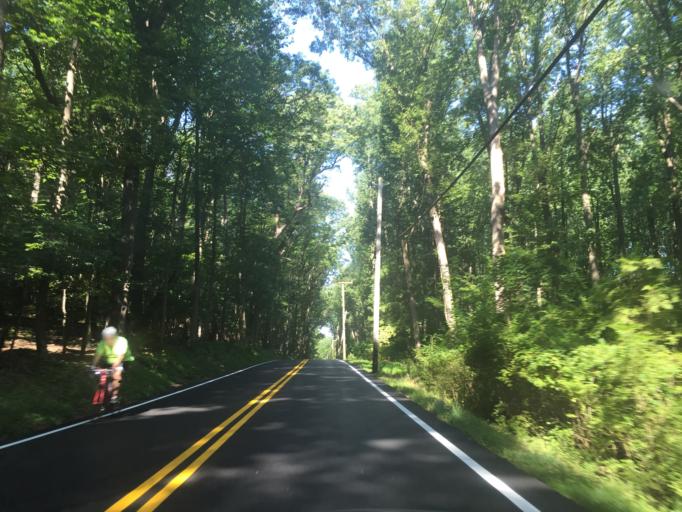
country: US
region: Maryland
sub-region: Baltimore County
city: Mays Chapel
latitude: 39.4130
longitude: -76.6715
